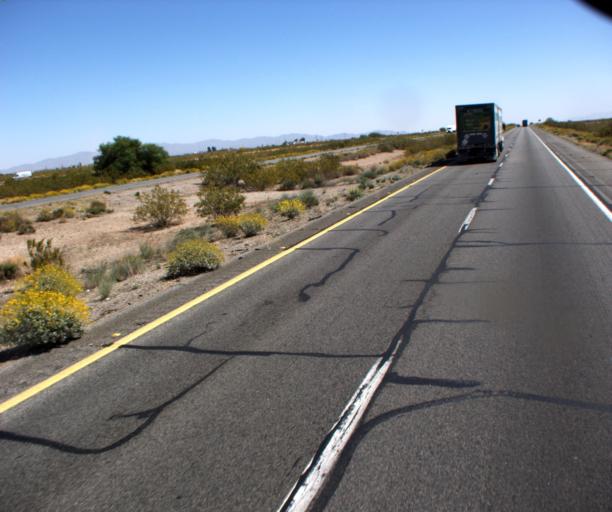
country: US
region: Arizona
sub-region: Maricopa County
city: Buckeye
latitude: 33.4817
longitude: -112.8674
